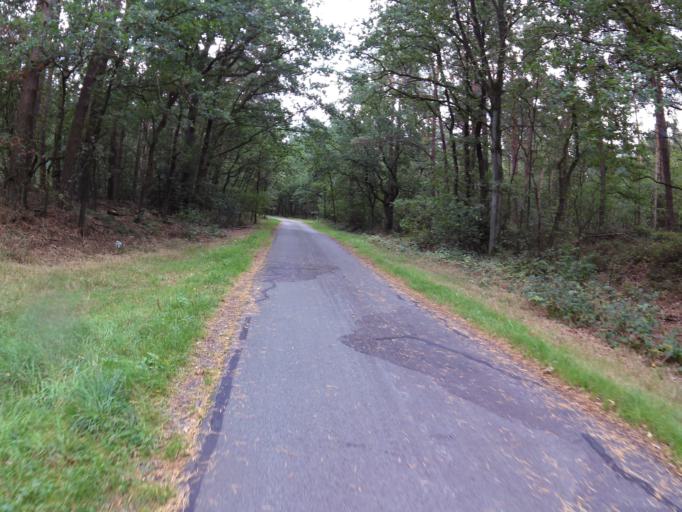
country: DE
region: Lower Saxony
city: Selsingen
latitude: 53.3634
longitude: 9.1679
